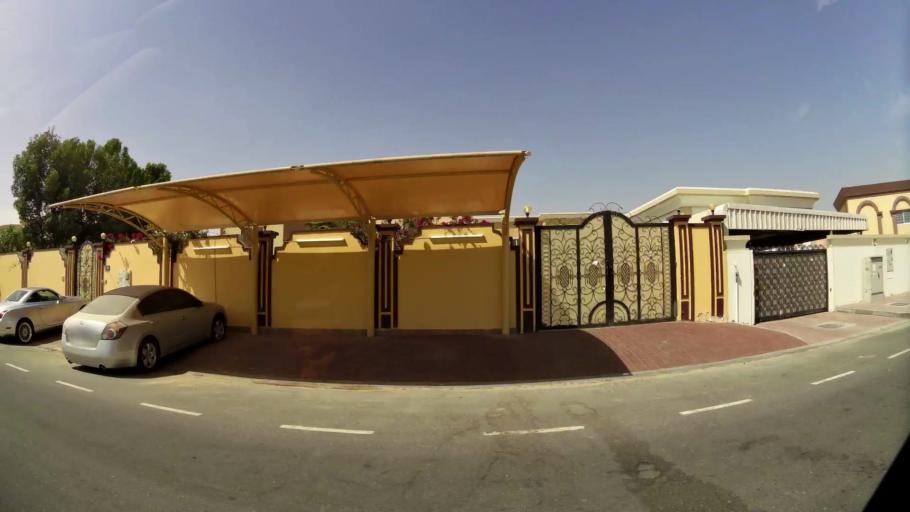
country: AE
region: Ash Shariqah
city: Sharjah
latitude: 25.2031
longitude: 55.4242
